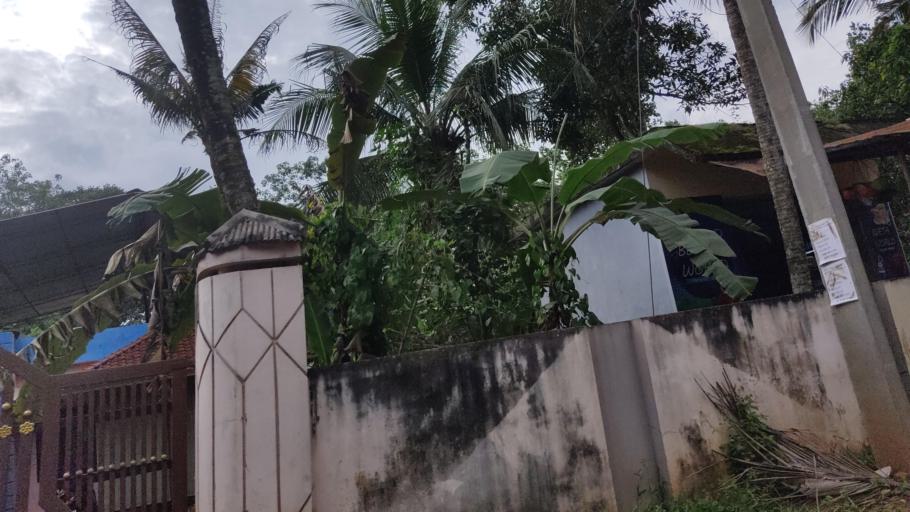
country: IN
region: Kerala
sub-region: Pattanamtitta
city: Pathanamthitta
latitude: 9.2359
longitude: 76.7792
